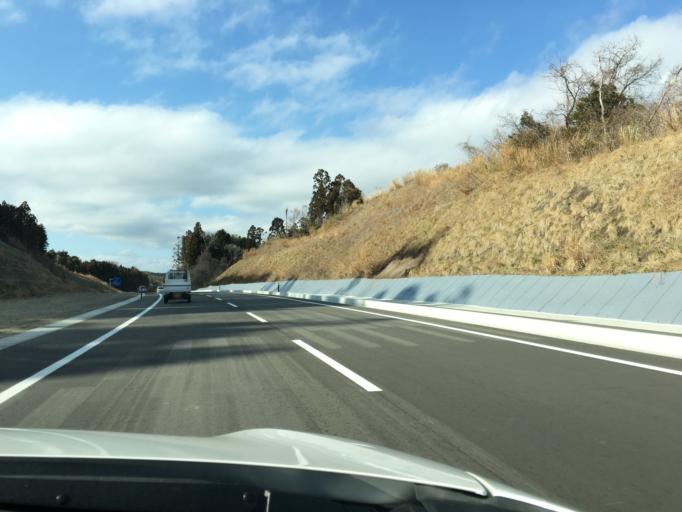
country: JP
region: Fukushima
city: Iwaki
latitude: 37.1356
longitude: 140.9948
